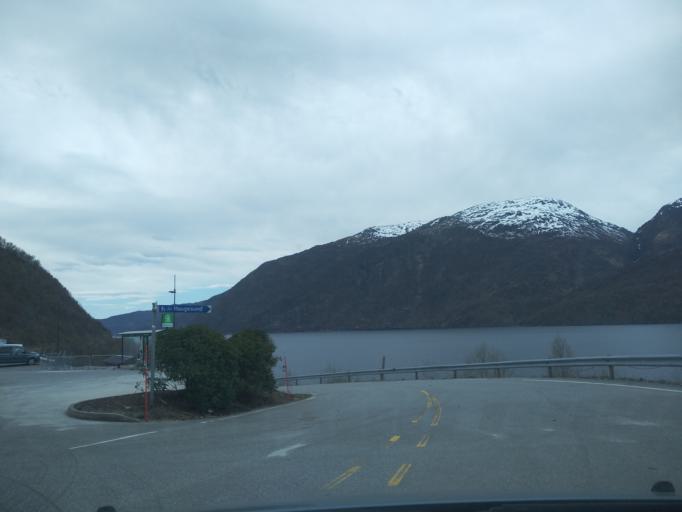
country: NO
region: Rogaland
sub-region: Sauda
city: Sauda
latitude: 59.8040
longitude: 6.2145
